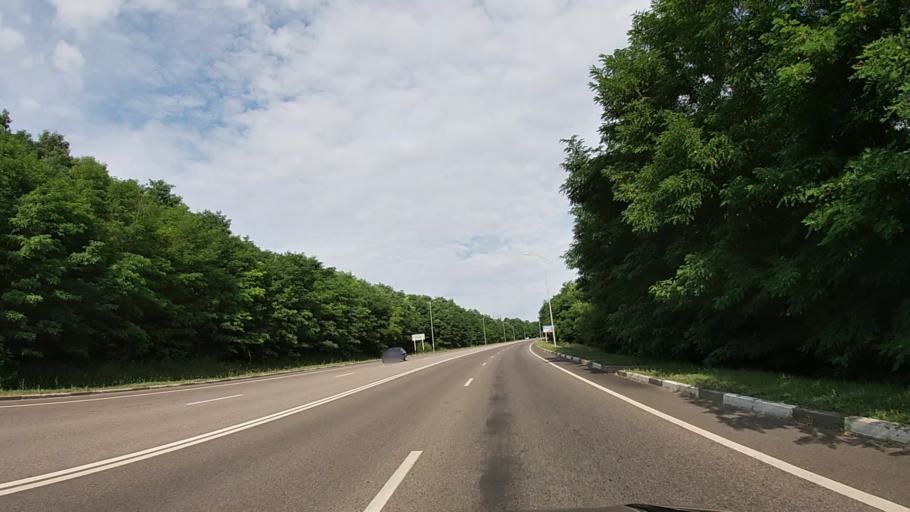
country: RU
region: Belgorod
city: Severnyy
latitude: 50.6357
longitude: 36.4571
